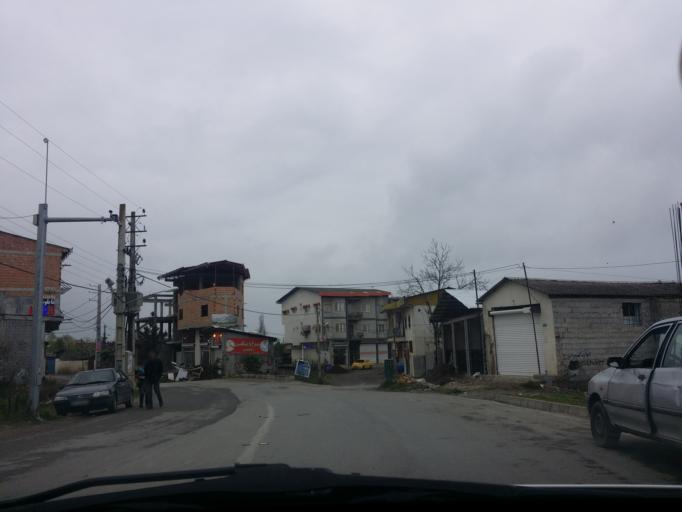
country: IR
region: Mazandaran
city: Chalus
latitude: 36.6655
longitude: 51.3898
